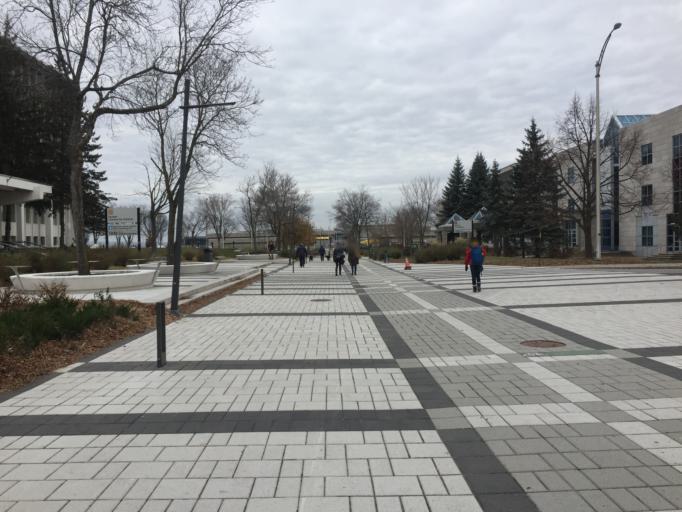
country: CA
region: Quebec
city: Quebec
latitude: 46.7815
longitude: -71.2740
